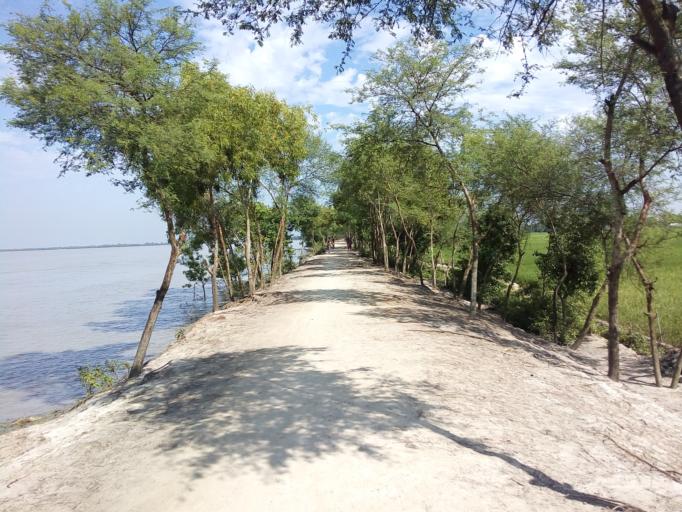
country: BD
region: Khulna
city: Phultala
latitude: 22.5299
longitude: 89.4180
